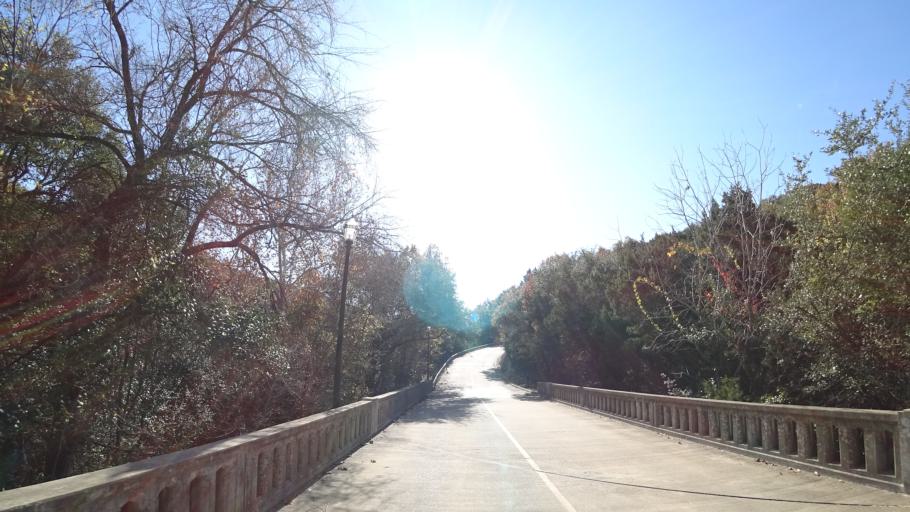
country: US
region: Texas
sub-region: Williamson County
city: Jollyville
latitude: 30.3819
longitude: -97.7675
